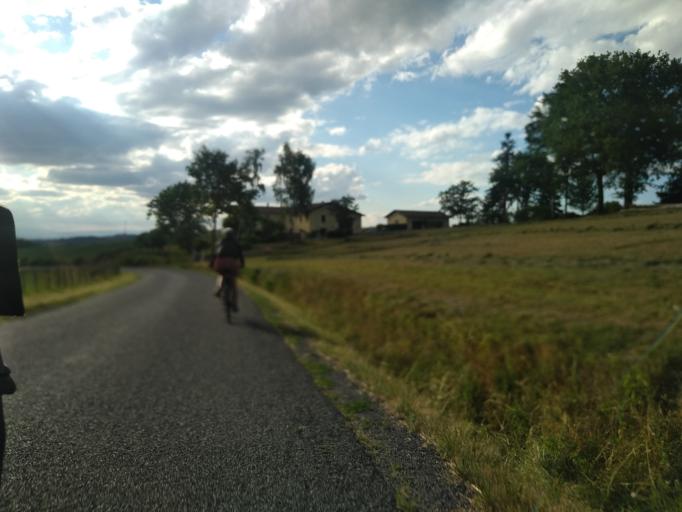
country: FR
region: Rhone-Alpes
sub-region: Departement du Rhone
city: Haute-Rivoire
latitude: 45.7256
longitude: 4.3536
